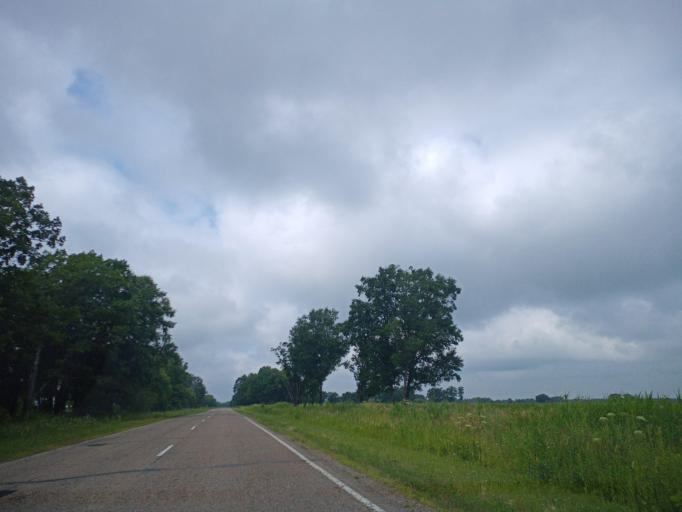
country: RU
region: Primorskiy
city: Dal'nerechensk
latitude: 45.9480
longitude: 133.9028
